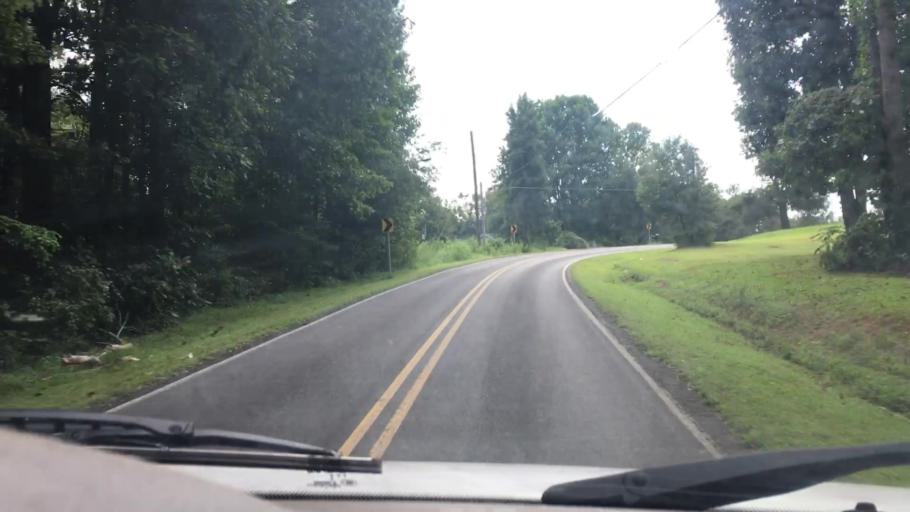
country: US
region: North Carolina
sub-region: Iredell County
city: Mooresville
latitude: 35.6691
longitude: -80.7846
